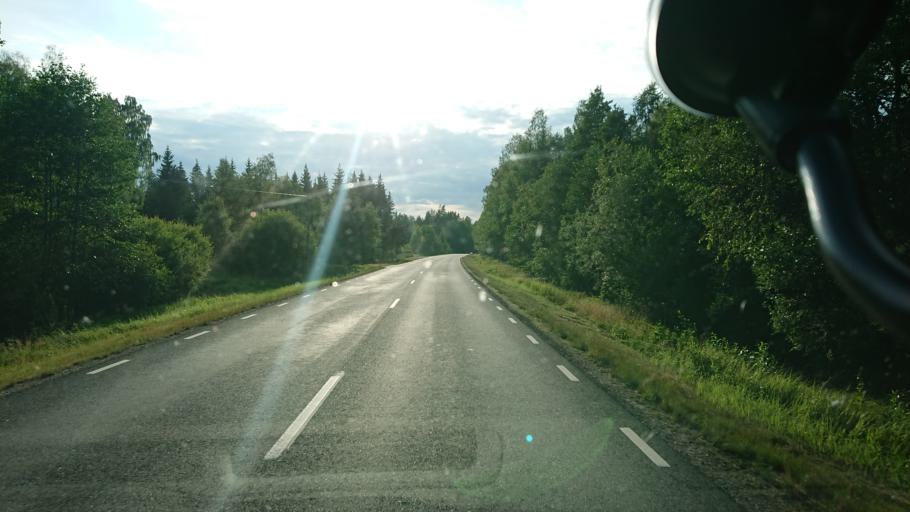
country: SE
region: Kronoberg
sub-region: Vaxjo Kommun
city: Rottne
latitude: 57.0345
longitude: 14.9298
